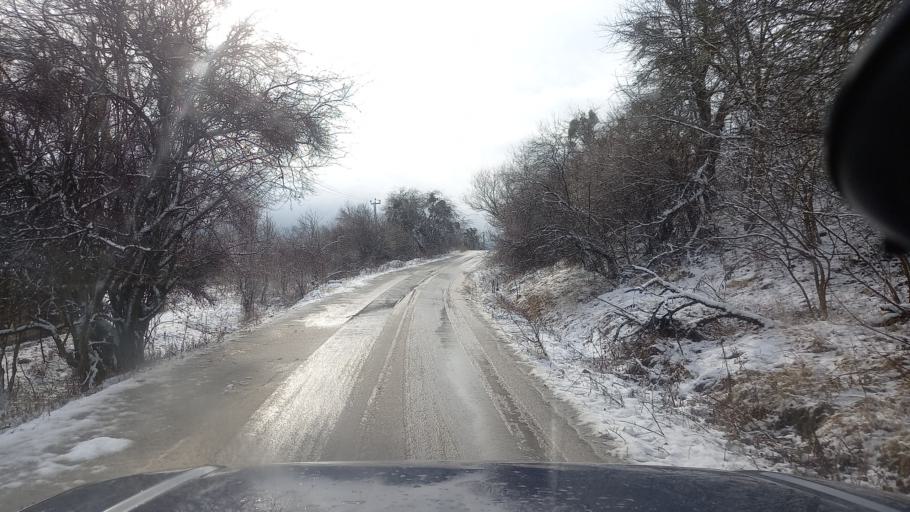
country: RU
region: Adygeya
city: Kamennomostskiy
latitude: 44.2343
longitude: 40.1928
